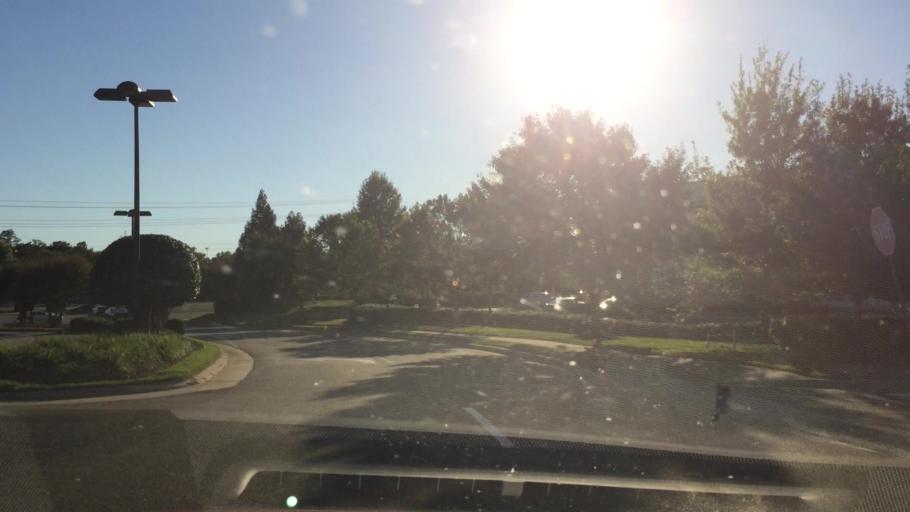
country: US
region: Virginia
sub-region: Henrico County
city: Short Pump
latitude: 37.6562
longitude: -77.6248
